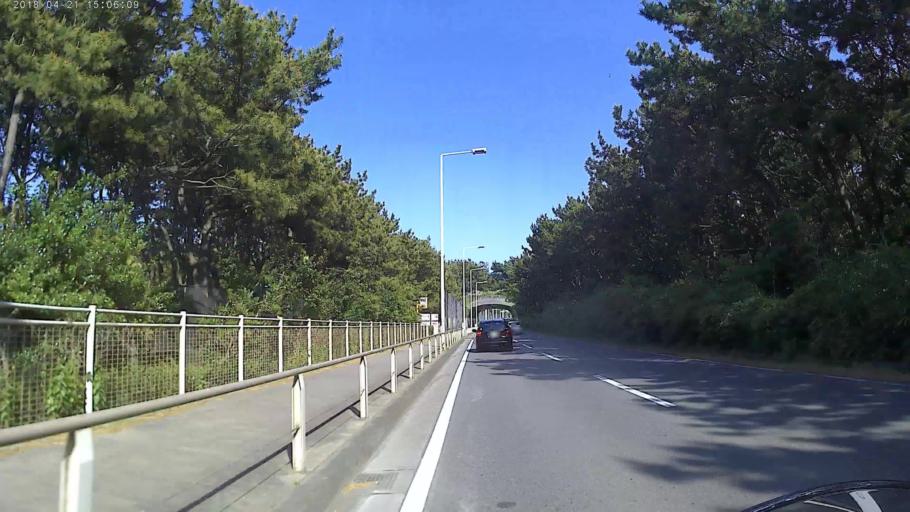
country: JP
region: Kanagawa
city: Fujisawa
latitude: 35.3206
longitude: 139.4453
